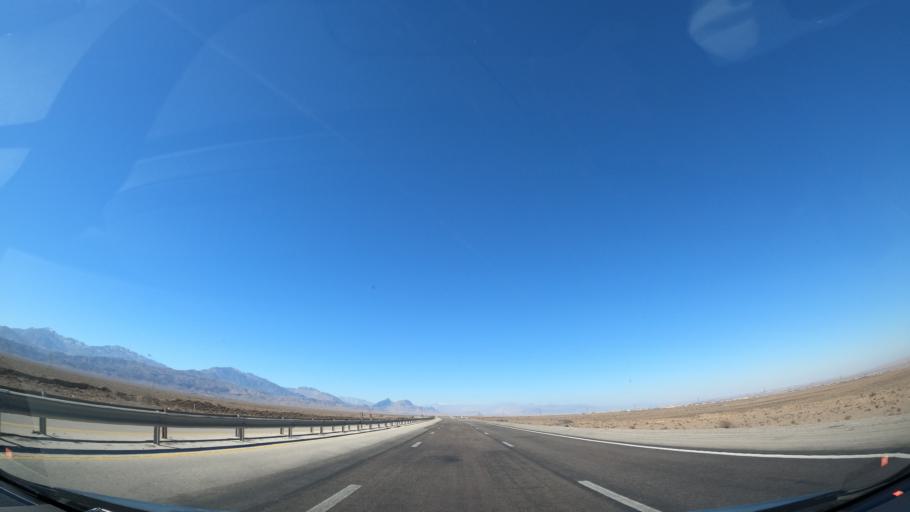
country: IR
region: Isfahan
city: Kashan
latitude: 33.8492
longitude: 51.5567
